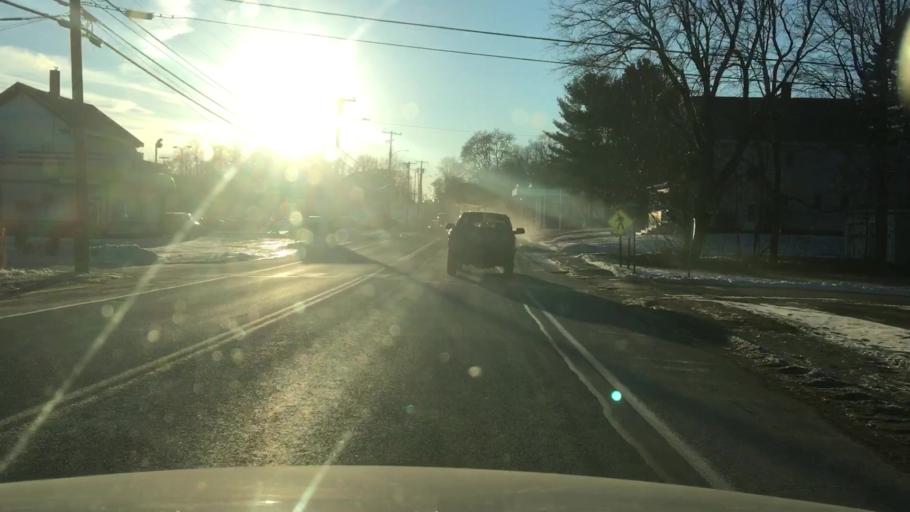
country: US
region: Maine
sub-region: Penobscot County
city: Brewer
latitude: 44.8009
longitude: -68.7532
